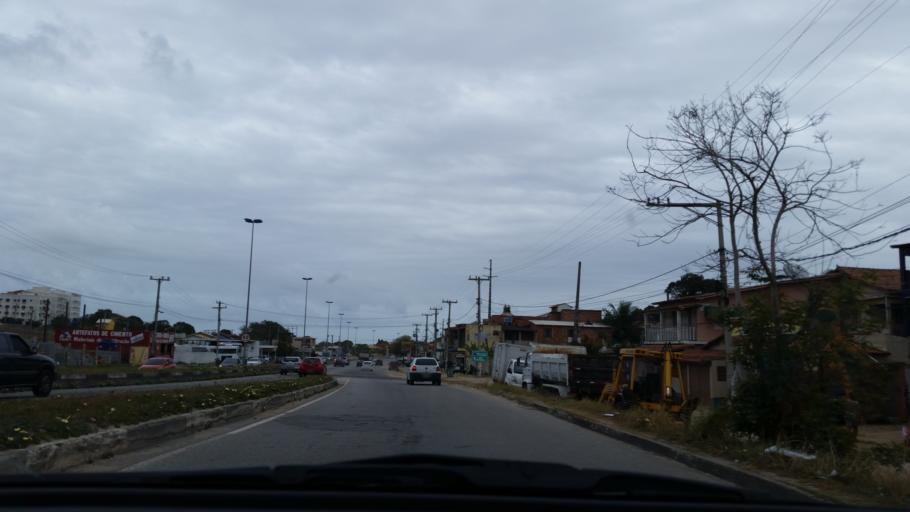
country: BR
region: Rio de Janeiro
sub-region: Cabo Frio
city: Cabo Frio
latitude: -22.8548
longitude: -42.0550
